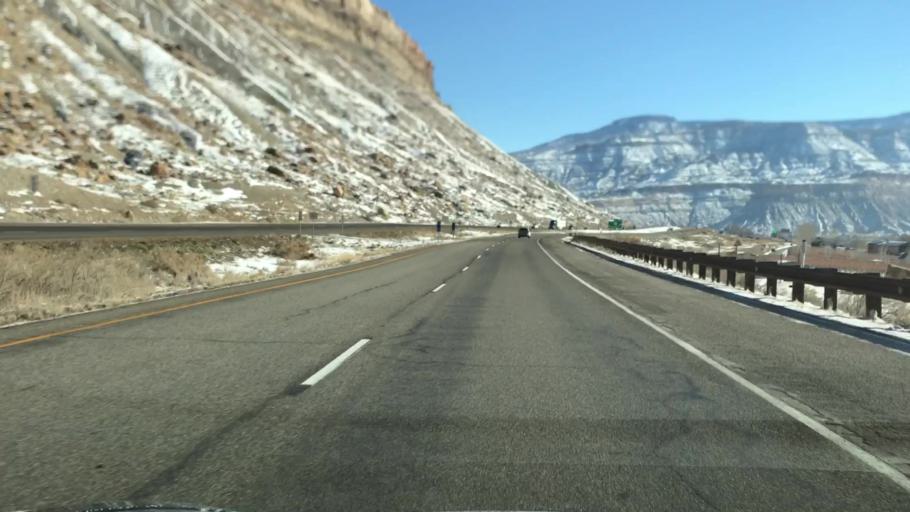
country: US
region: Colorado
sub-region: Mesa County
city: Palisade
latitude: 39.1202
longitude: -108.3683
